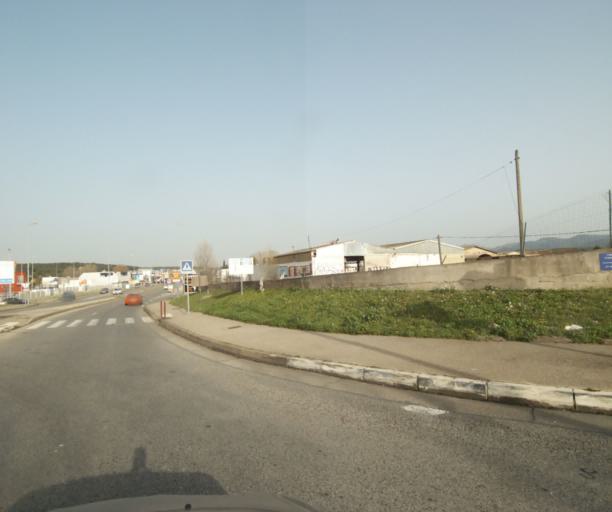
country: FR
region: Provence-Alpes-Cote d'Azur
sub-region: Departement des Bouches-du-Rhone
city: Septemes-les-Vallons
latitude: 43.4151
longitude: 5.3518
